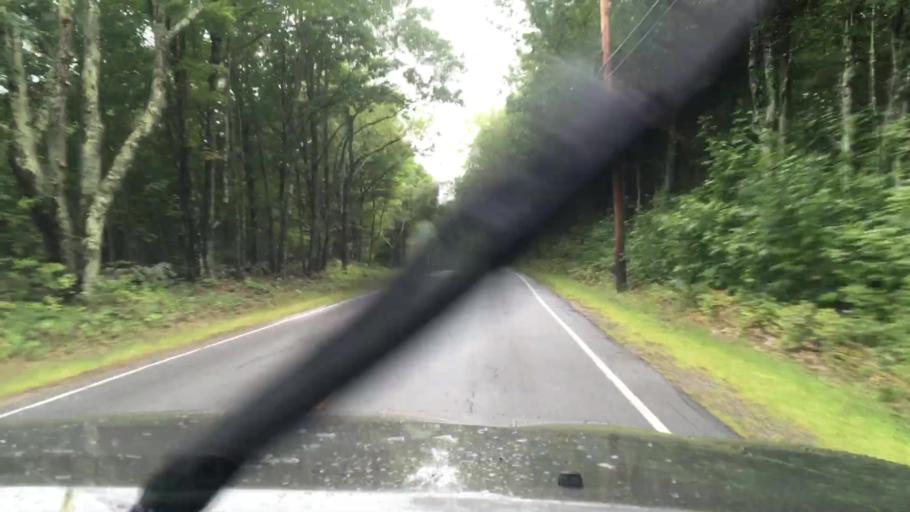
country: US
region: New Hampshire
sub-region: Belknap County
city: Meredith
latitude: 43.6424
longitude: -71.5335
